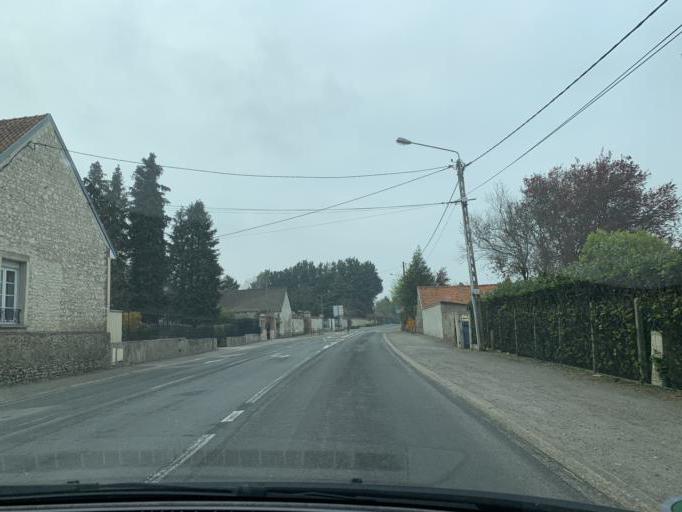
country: FR
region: Nord-Pas-de-Calais
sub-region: Departement du Pas-de-Calais
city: Montreuil
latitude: 50.4049
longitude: 1.7253
